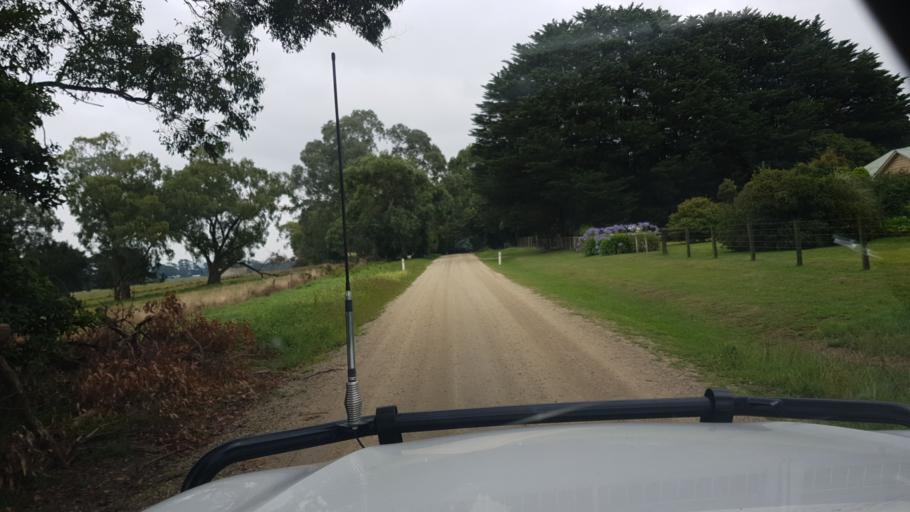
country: AU
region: Victoria
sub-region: Baw Baw
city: Warragul
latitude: -38.1182
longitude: 146.0087
